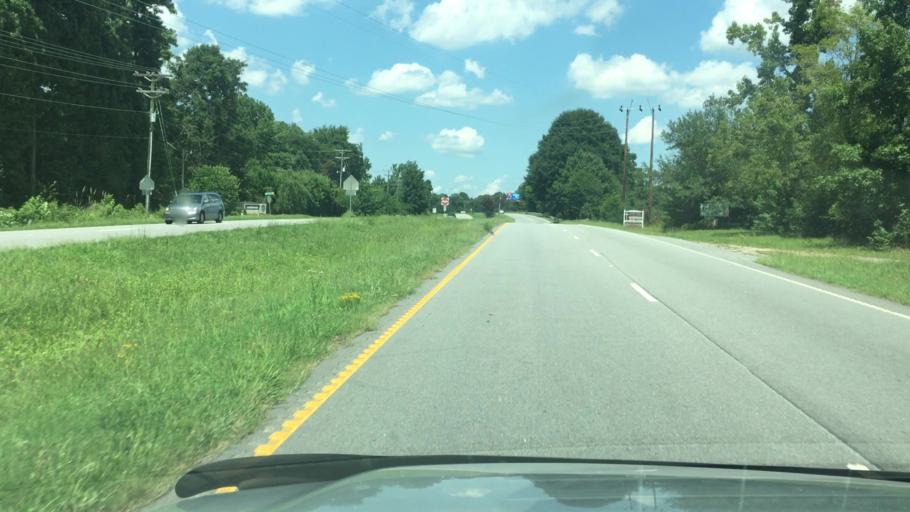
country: US
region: South Carolina
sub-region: Spartanburg County
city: Roebuck
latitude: 34.8596
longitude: -81.9631
